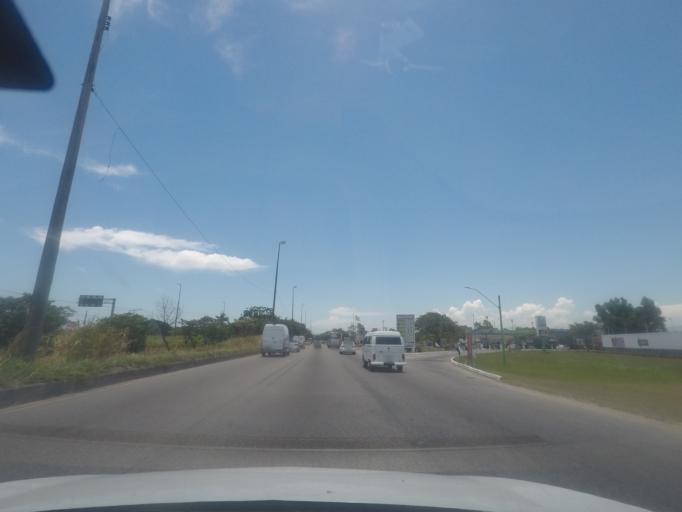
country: BR
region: Rio de Janeiro
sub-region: Itaguai
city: Itaguai
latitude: -22.8921
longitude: -43.6711
